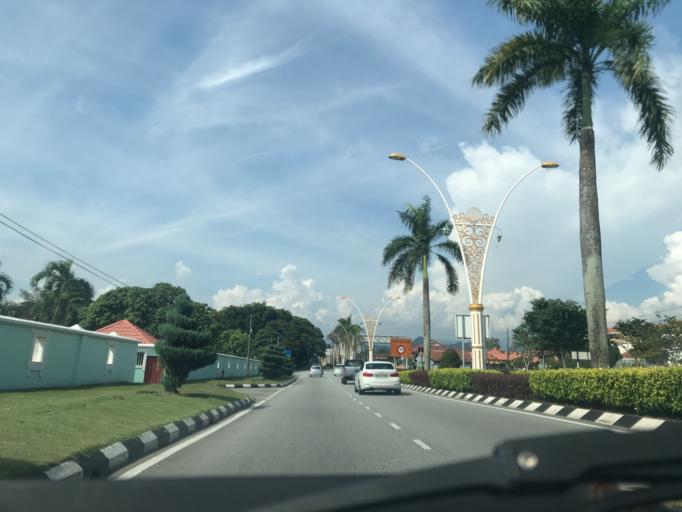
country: MY
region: Perak
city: Ipoh
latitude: 4.5927
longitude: 101.0913
